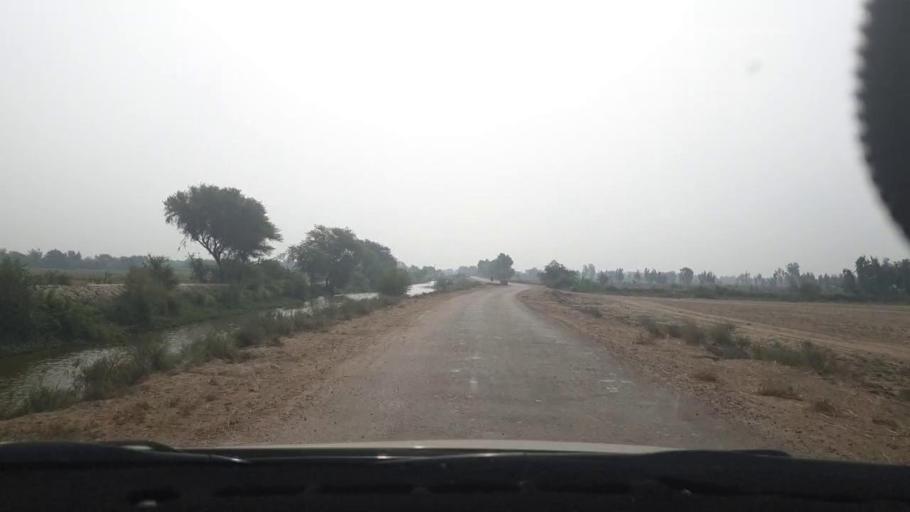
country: PK
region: Sindh
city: Tando Muhammad Khan
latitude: 25.0535
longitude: 68.5496
